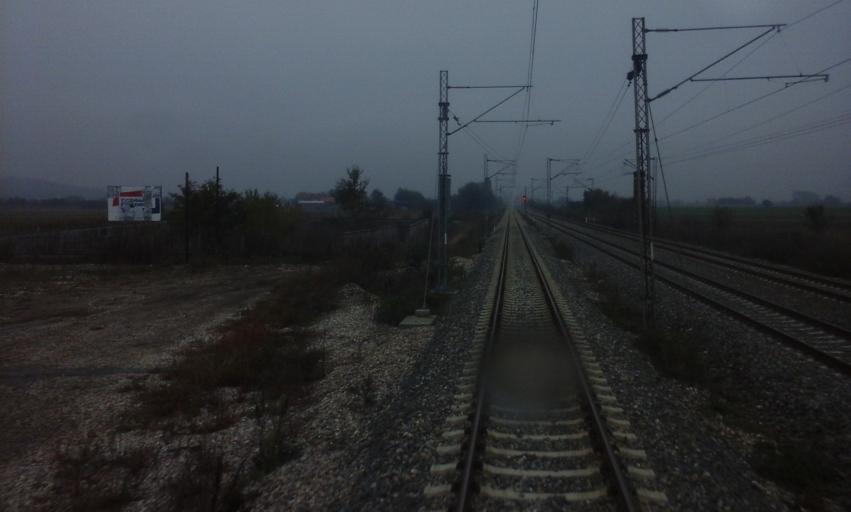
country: RS
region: Central Serbia
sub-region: Pomoravski Okrug
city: Paracin
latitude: 43.8845
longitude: 21.3844
